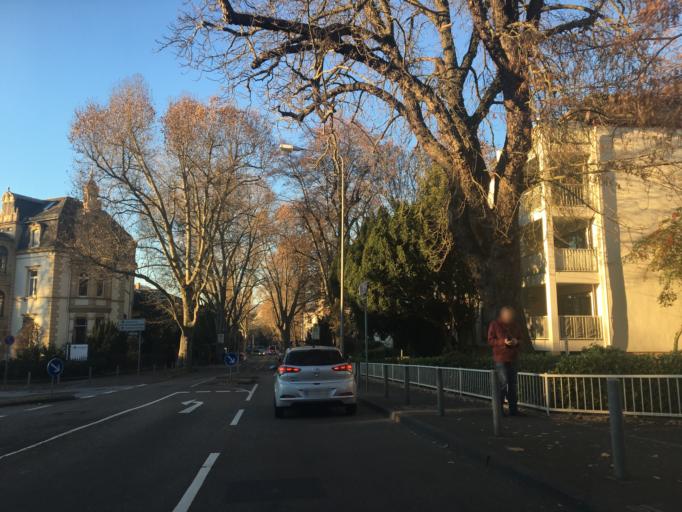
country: DE
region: Hesse
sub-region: Regierungsbezirk Darmstadt
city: Wiesbaden
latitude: 50.0781
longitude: 8.2493
